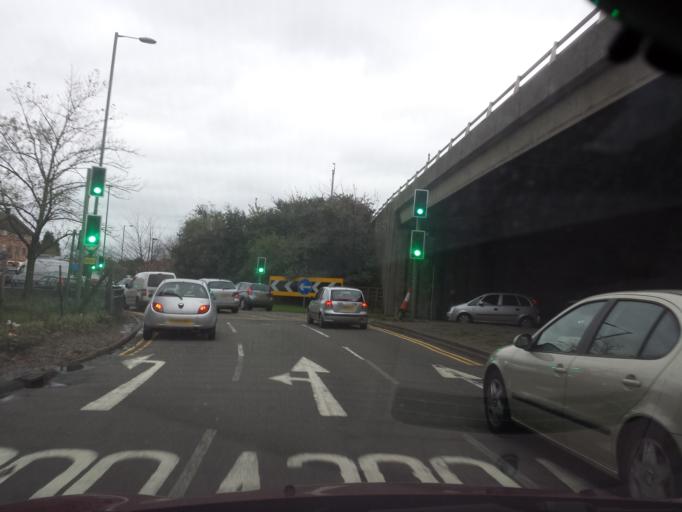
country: GB
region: England
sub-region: Surrey
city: Sunbury-on-Thames
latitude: 51.4188
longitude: -0.4202
